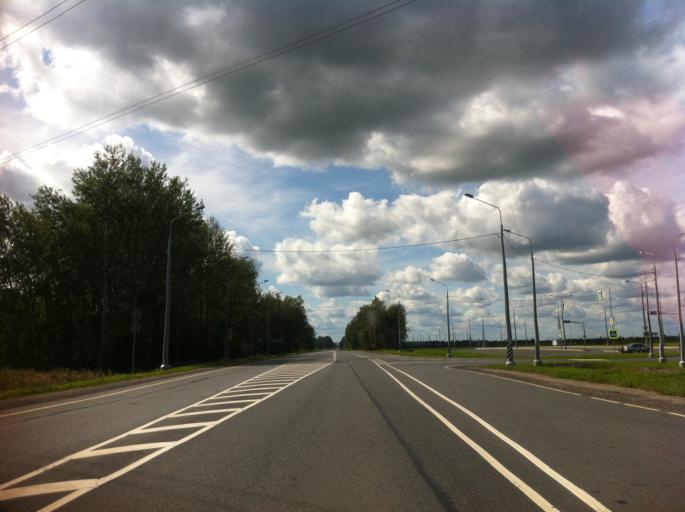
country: RU
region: Pskov
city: Pskov
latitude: 57.7747
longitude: 28.1424
